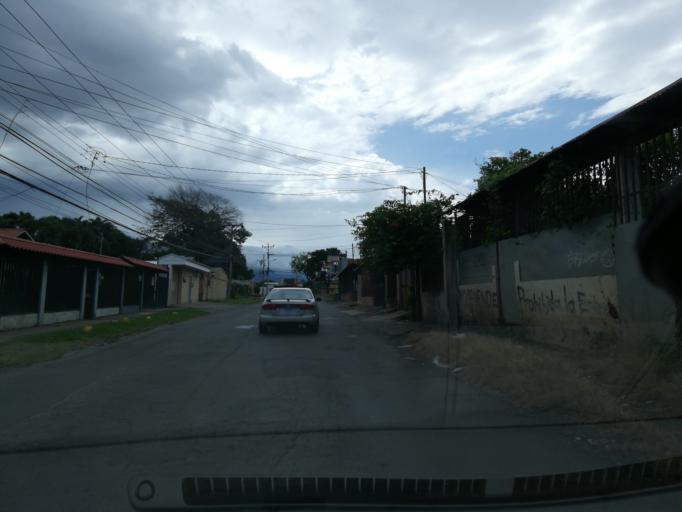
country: CR
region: Alajuela
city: Alajuela
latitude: 9.9934
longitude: -84.2315
